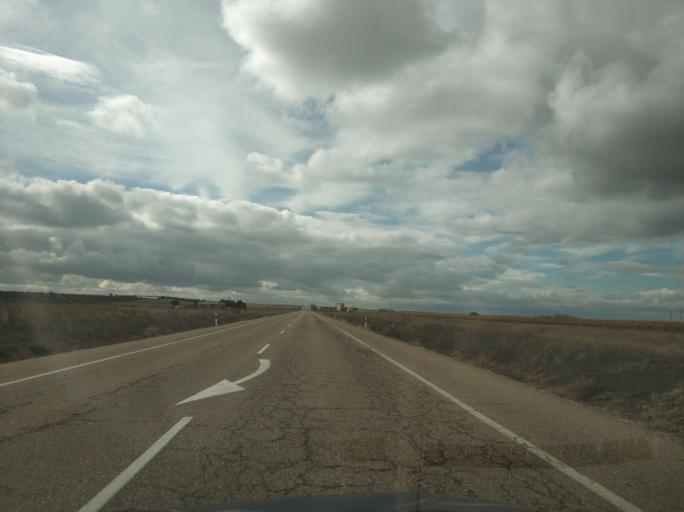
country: ES
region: Castille and Leon
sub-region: Provincia de Valladolid
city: Pollos
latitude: 41.4265
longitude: -5.1148
